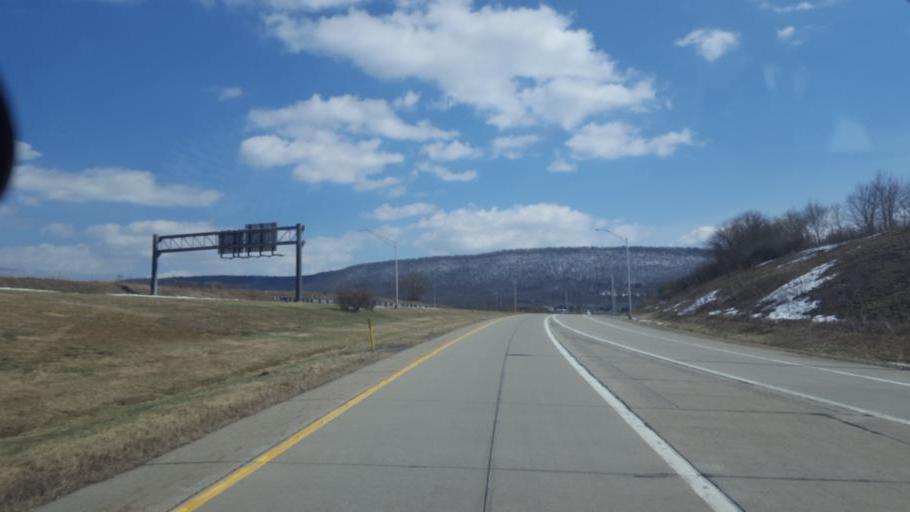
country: US
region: Pennsylvania
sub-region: Centre County
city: Pleasant Gap
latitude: 40.8886
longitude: -77.7295
